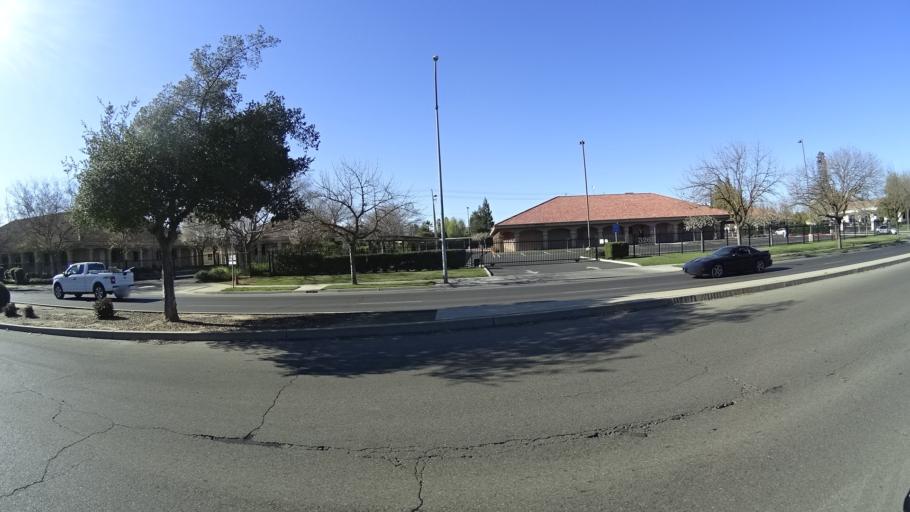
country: US
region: California
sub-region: Fresno County
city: Fresno
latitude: 36.8236
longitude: -119.8510
